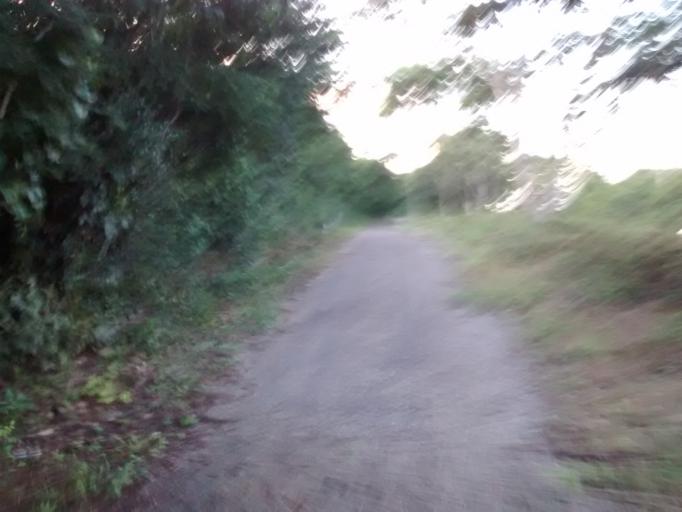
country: MX
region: Yucatan
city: Valladolid
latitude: 20.6950
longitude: -88.2286
